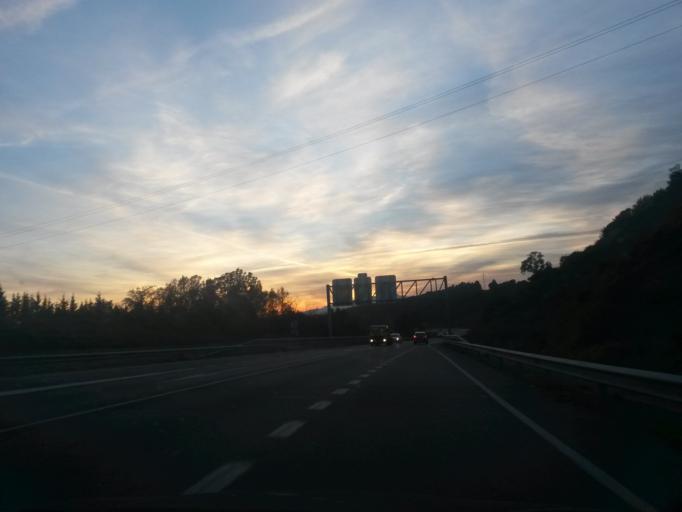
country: ES
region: Catalonia
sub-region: Provincia de Girona
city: Quart d'Onyar
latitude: 41.9602
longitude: 2.8448
